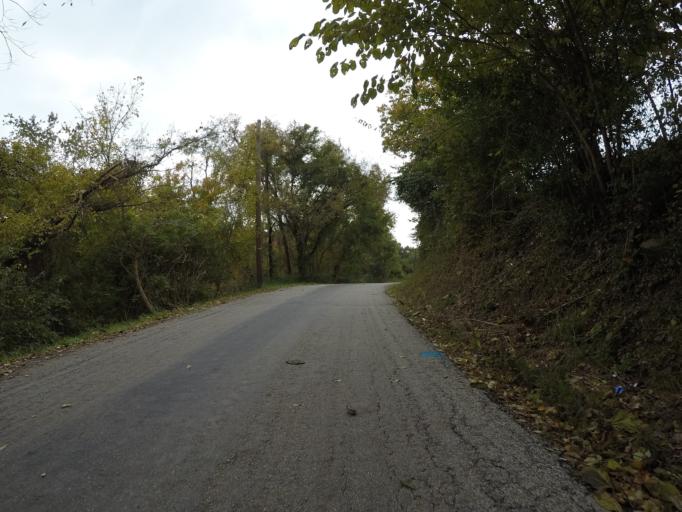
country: US
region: West Virginia
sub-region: Wayne County
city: Lavalette
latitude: 38.3633
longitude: -82.4208
